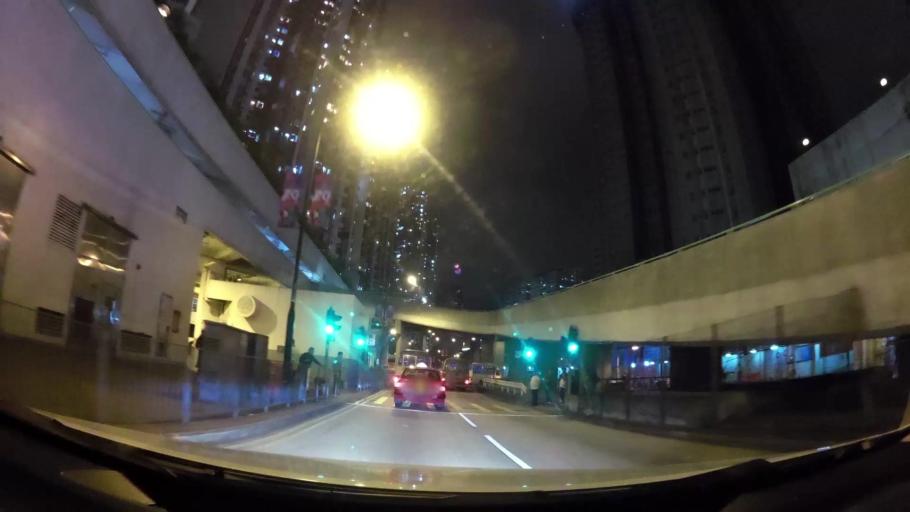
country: HK
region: Tsuen Wan
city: Tsuen Wan
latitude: 22.3561
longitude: 114.1280
